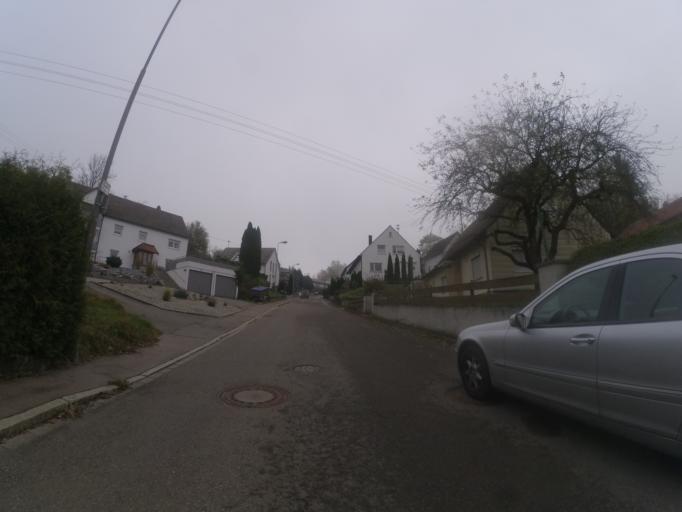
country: DE
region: Baden-Wuerttemberg
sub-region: Tuebingen Region
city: Staig
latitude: 48.3360
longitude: 10.0034
